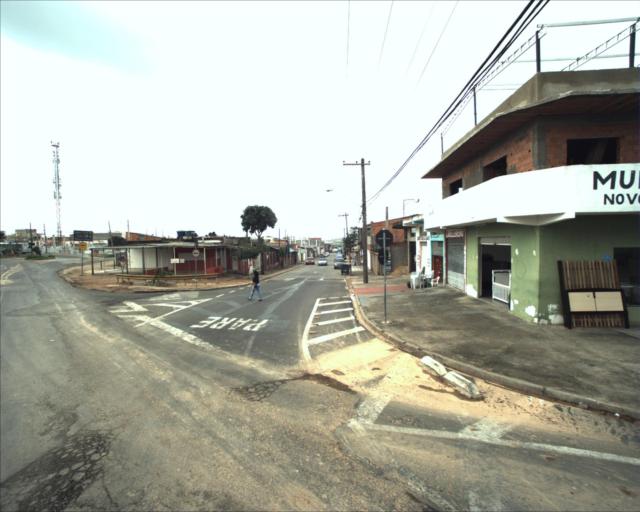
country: BR
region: Sao Paulo
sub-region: Sorocaba
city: Sorocaba
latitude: -23.4319
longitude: -47.4670
